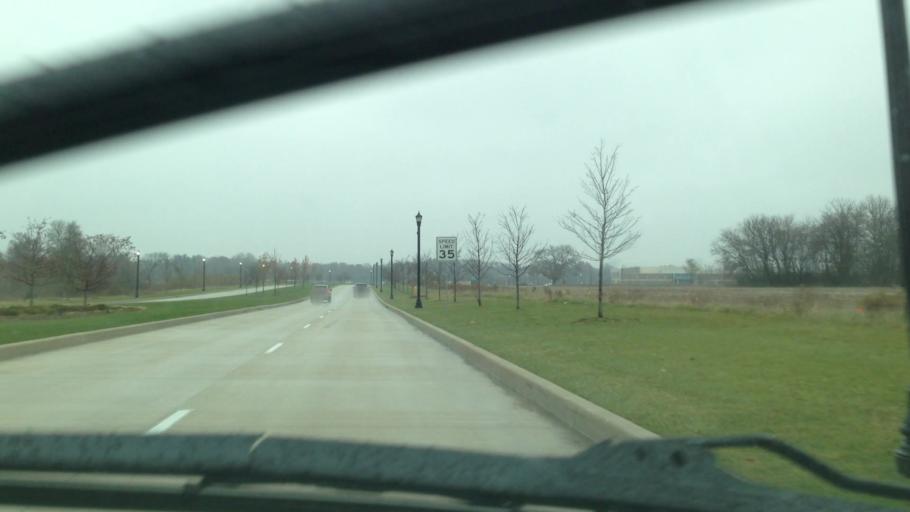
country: US
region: Indiana
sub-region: Saint Joseph County
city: Granger
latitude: 41.7288
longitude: -86.1517
